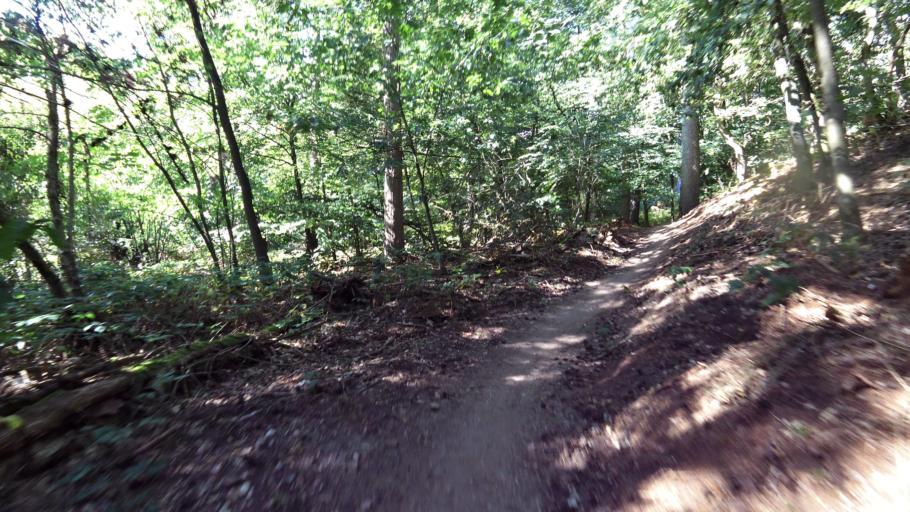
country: NL
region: Gelderland
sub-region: Gemeente Renkum
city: Doorwerth
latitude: 51.9767
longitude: 5.8083
